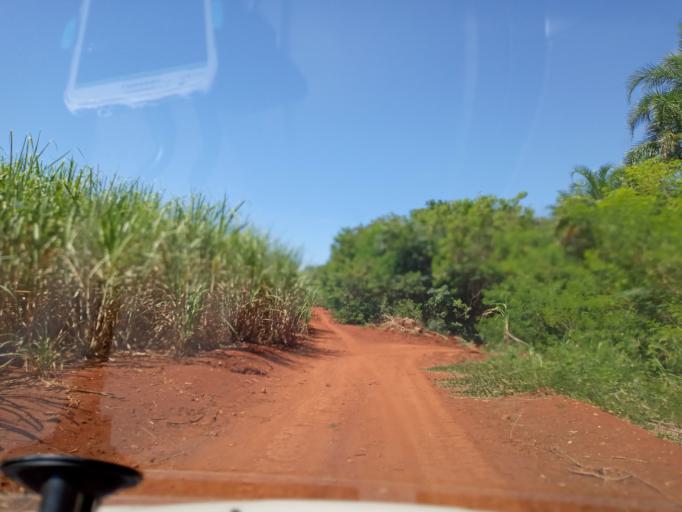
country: BR
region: Goias
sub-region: Itumbiara
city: Itumbiara
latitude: -18.4396
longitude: -49.1423
